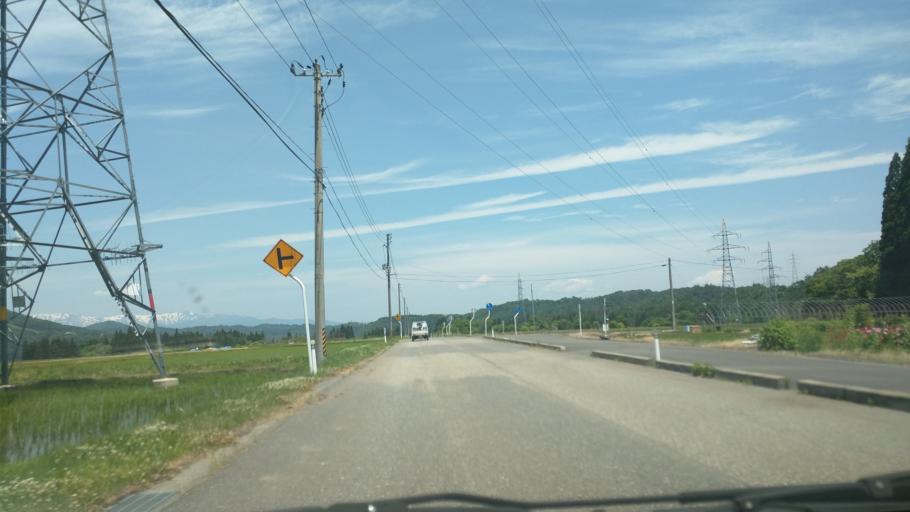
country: JP
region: Fukushima
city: Kitakata
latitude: 37.5118
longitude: 139.7182
